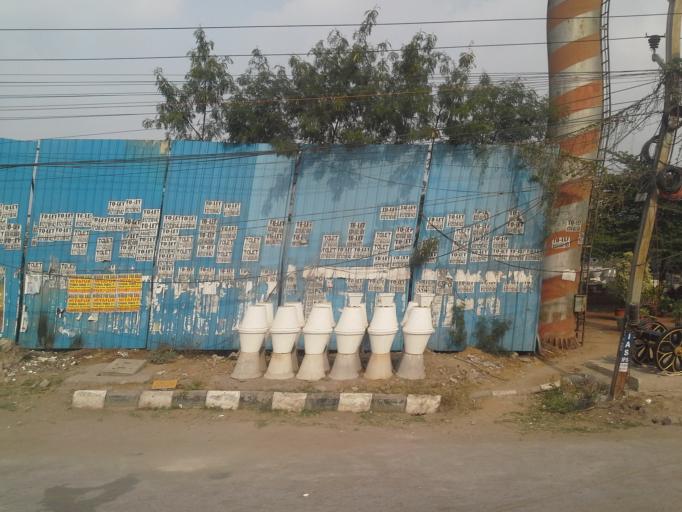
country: IN
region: Telangana
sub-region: Rangareddi
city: Kukatpalli
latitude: 17.4553
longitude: 78.3780
